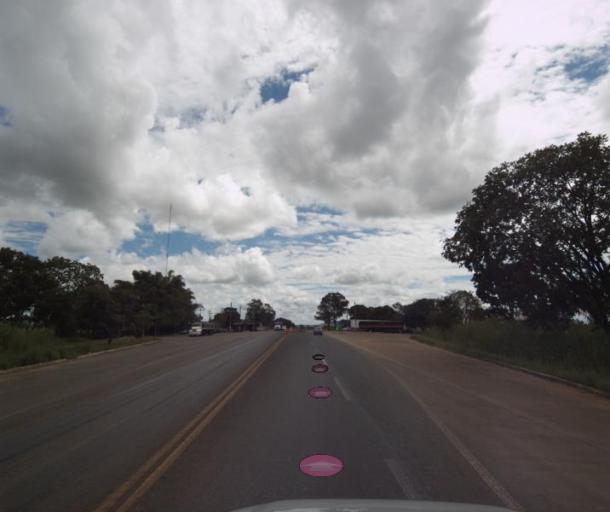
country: BR
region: Goias
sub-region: Uruacu
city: Uruacu
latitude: -14.4709
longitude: -49.1560
